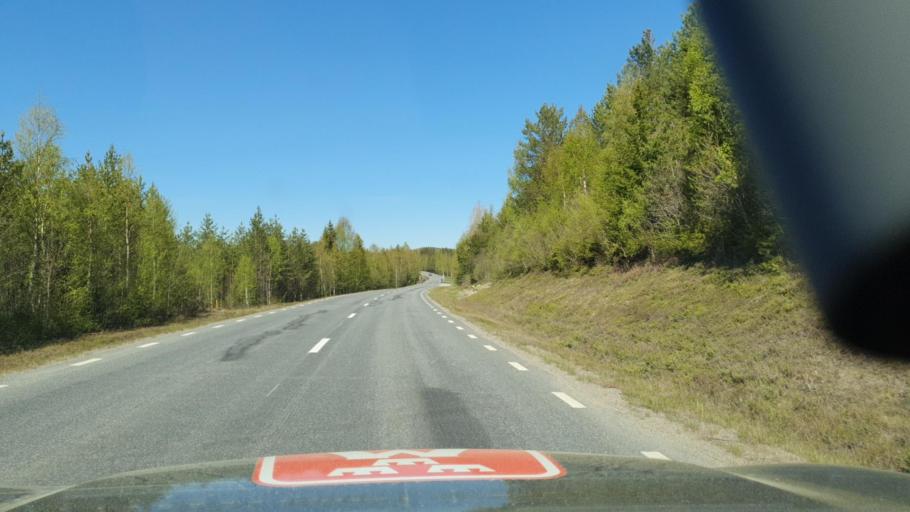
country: SE
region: Vaesternorrland
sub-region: OErnskoeldsviks Kommun
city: Ornskoldsvik
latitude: 63.6987
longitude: 18.5086
